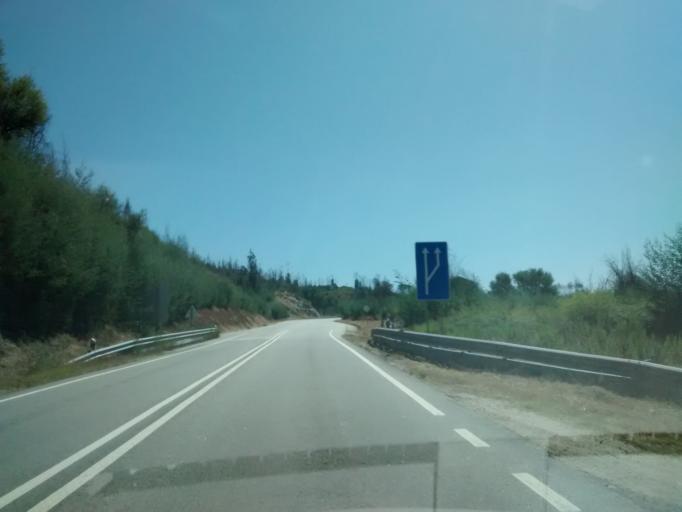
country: PT
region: Coimbra
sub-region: Tabua
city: Tabua
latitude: 40.3687
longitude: -8.0583
